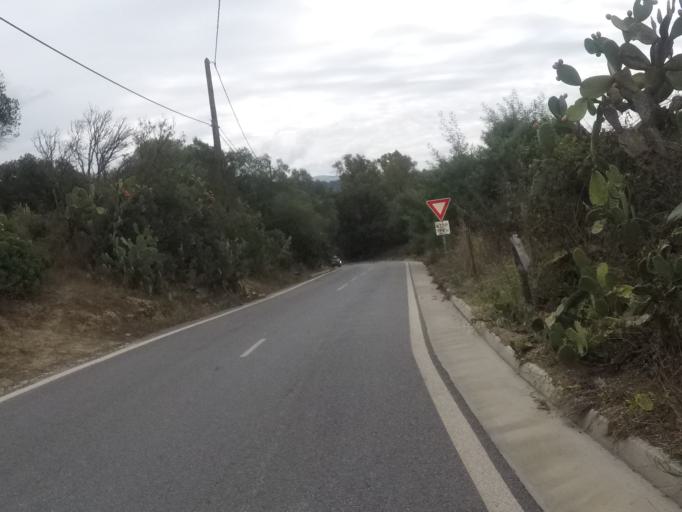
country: FR
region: Corsica
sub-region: Departement de la Corse-du-Sud
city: Propriano
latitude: 41.7294
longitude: 8.8290
